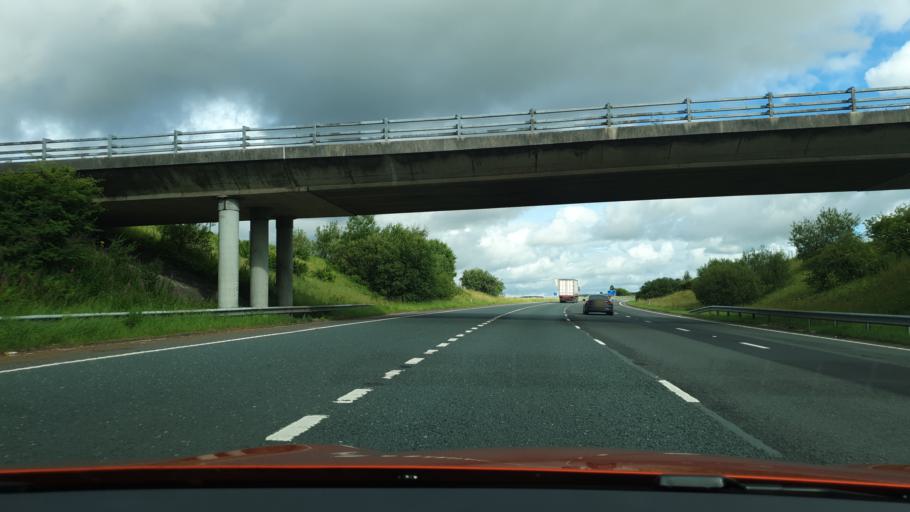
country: GB
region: England
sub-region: Cumbria
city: Sedbergh
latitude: 54.4523
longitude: -2.6122
